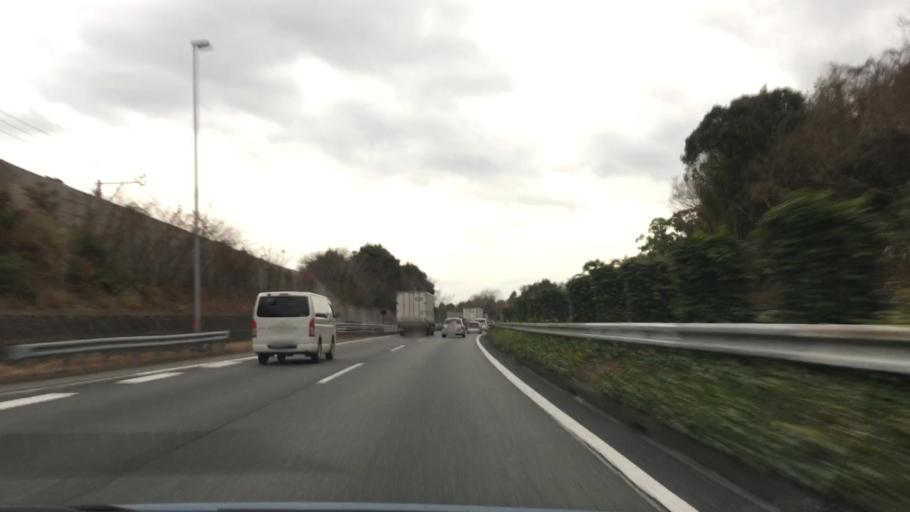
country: JP
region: Shizuoka
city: Fujinomiya
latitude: 35.1545
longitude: 138.6174
